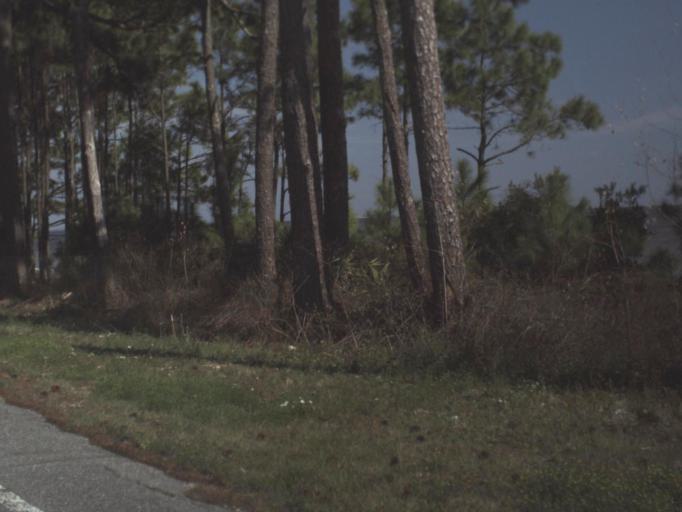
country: US
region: Florida
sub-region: Franklin County
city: Eastpoint
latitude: 29.7808
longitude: -84.7784
